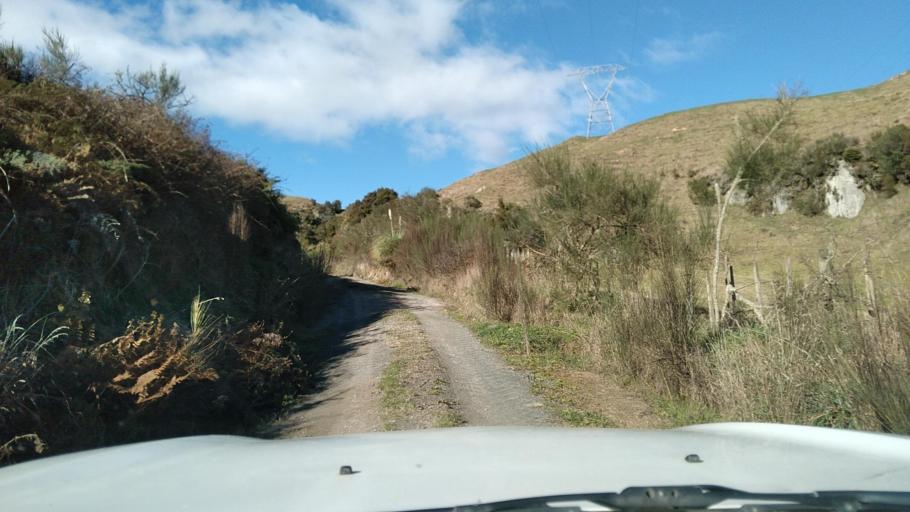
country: NZ
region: Waikato
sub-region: South Waikato District
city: Tokoroa
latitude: -38.3424
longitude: 175.6749
